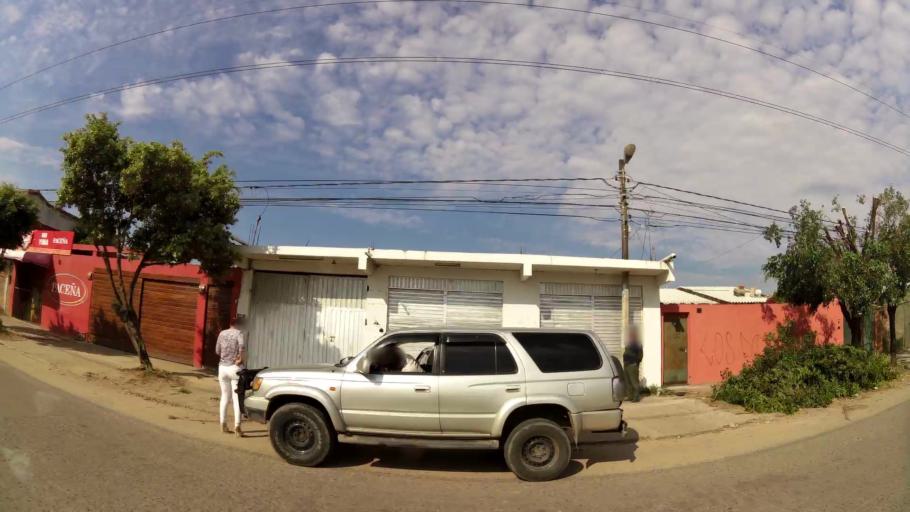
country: BO
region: Santa Cruz
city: Santa Cruz de la Sierra
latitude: -17.7263
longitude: -63.1629
